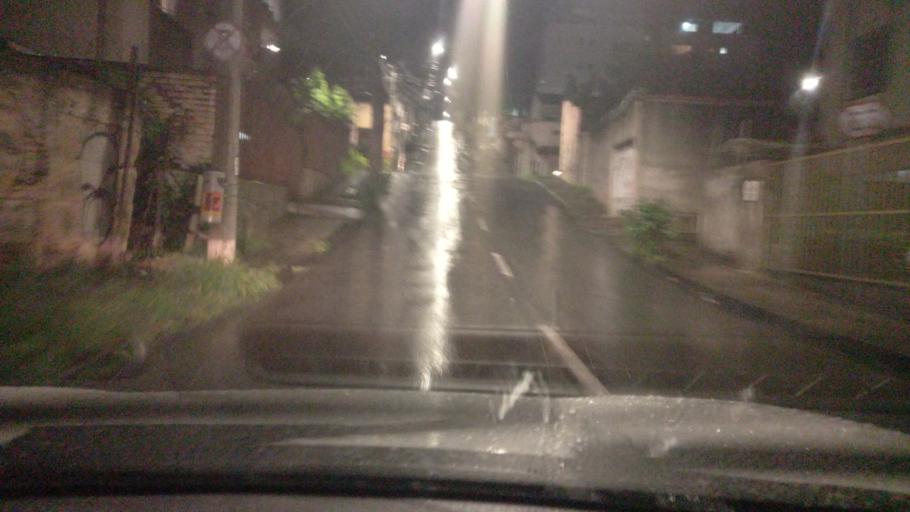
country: BR
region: Minas Gerais
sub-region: Belo Horizonte
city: Belo Horizonte
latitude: -19.9062
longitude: -43.9287
